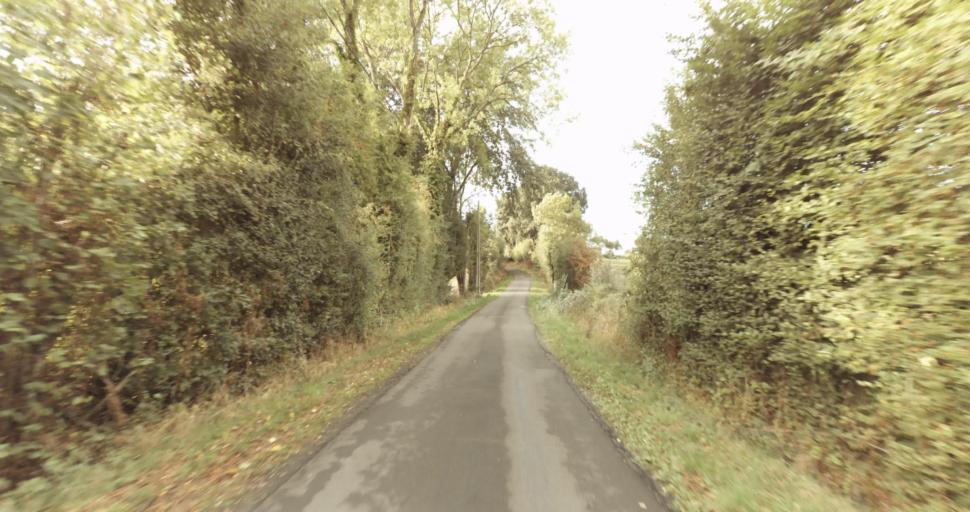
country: FR
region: Lower Normandy
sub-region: Departement de l'Orne
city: Sees
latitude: 48.6891
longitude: 0.2462
